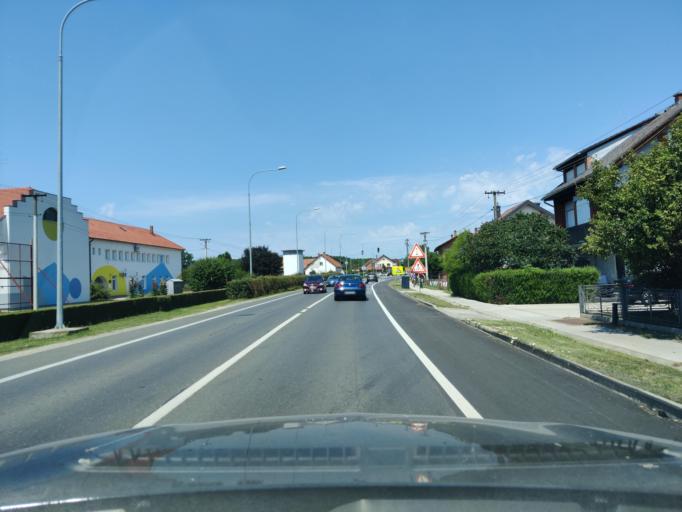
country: HR
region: Medimurska
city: Senkovec
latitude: 46.4037
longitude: 16.4213
